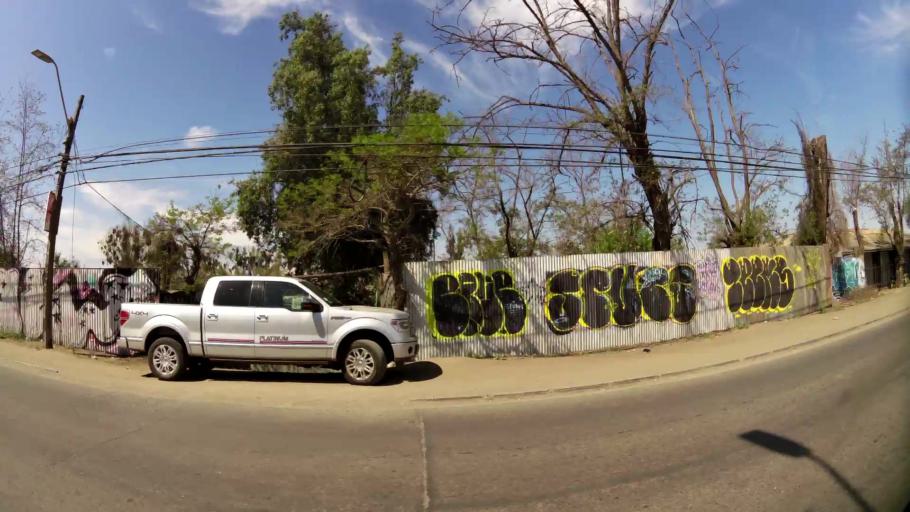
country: CL
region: Santiago Metropolitan
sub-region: Provincia de Santiago
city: Lo Prado
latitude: -33.4001
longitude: -70.7418
